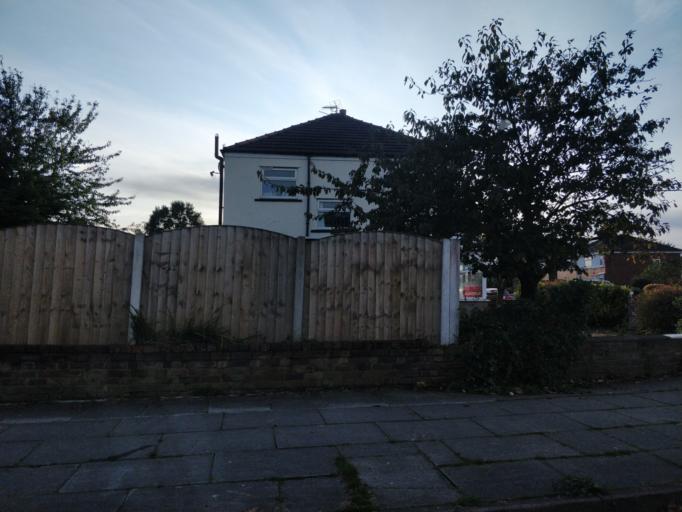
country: GB
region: England
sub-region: Lancashire
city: Banks
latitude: 53.6712
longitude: -2.9600
